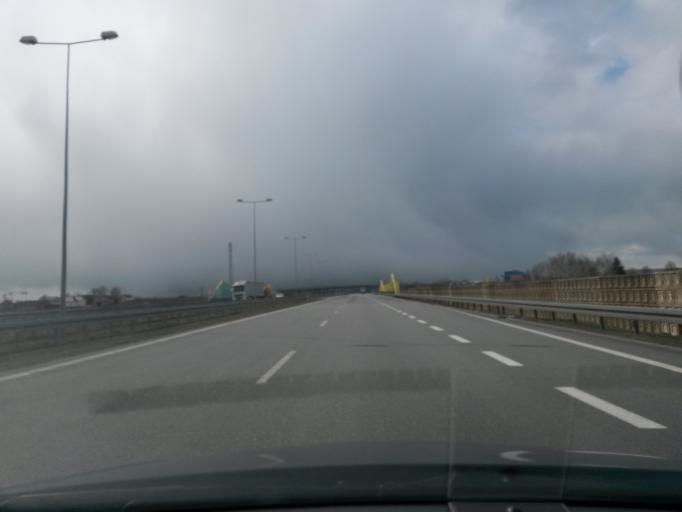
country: PL
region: Greater Poland Voivodeship
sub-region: Powiat koninski
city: Stare Miasto
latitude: 52.1619
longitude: 18.2194
